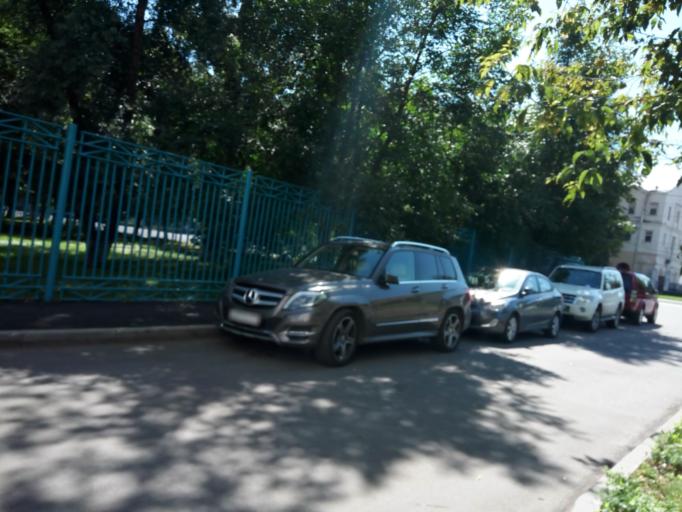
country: RU
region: Moscow
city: Sokol
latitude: 55.7777
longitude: 37.5282
